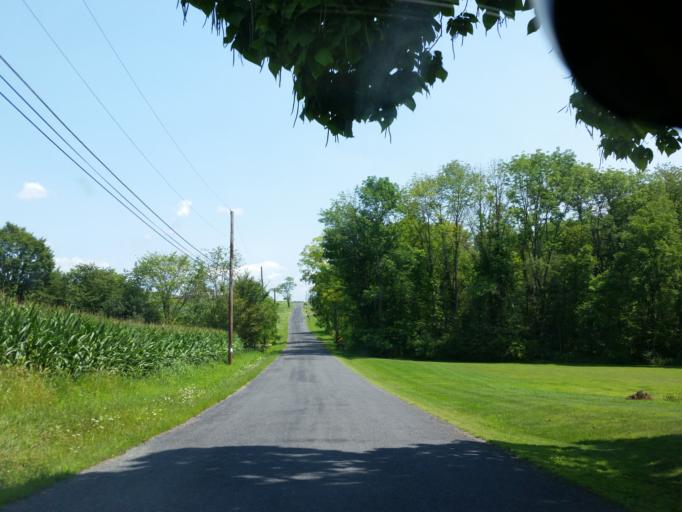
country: US
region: Pennsylvania
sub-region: Union County
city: New Columbia
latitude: 41.0407
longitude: -76.9468
